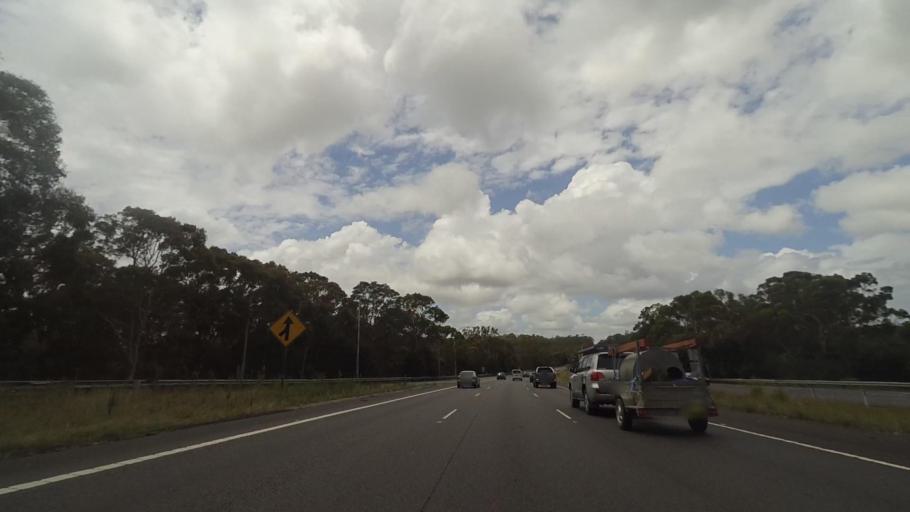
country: AU
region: New South Wales
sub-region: Gosford Shire
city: Umina
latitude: -33.4621
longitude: 151.1964
